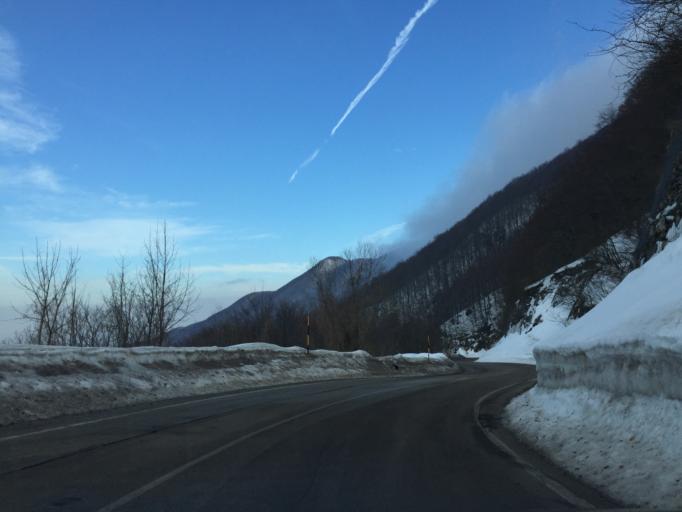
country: IT
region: Molise
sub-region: Provincia di Campobasso
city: San Massimo
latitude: 41.4684
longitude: 14.4002
